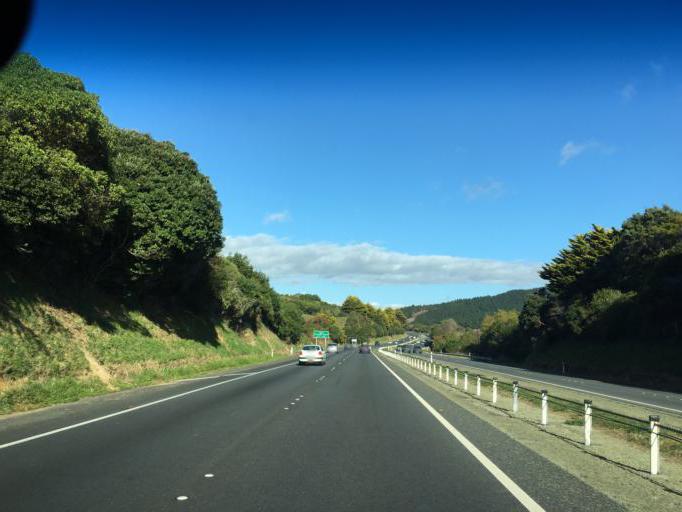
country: NZ
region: Wellington
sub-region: Porirua City
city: Porirua
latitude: -41.1751
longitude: 174.8305
